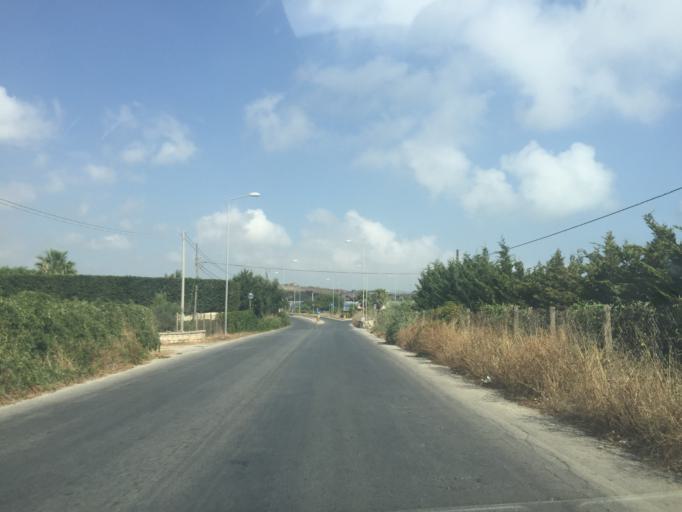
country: IT
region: Sicily
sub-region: Ragusa
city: Donnalucata
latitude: 36.7764
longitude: 14.6060
